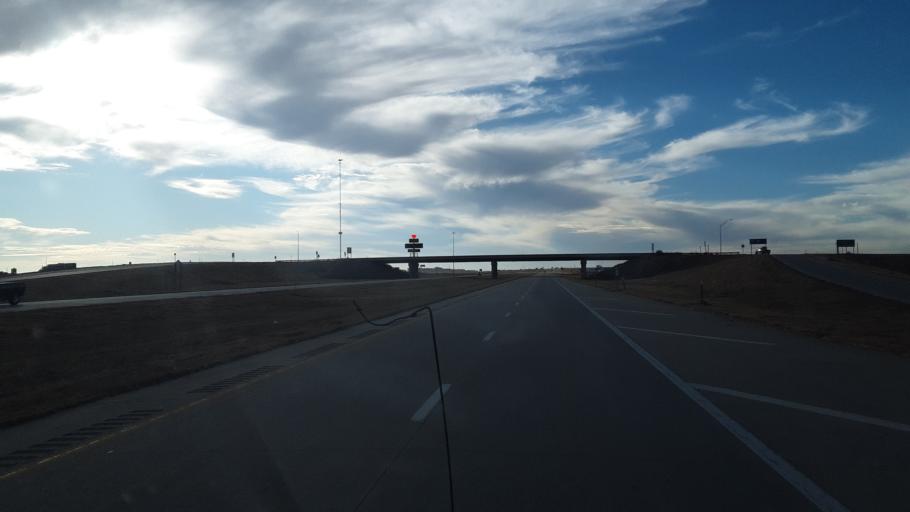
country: US
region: Kansas
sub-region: Finney County
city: Holcomb
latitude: 38.0033
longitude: -100.9909
